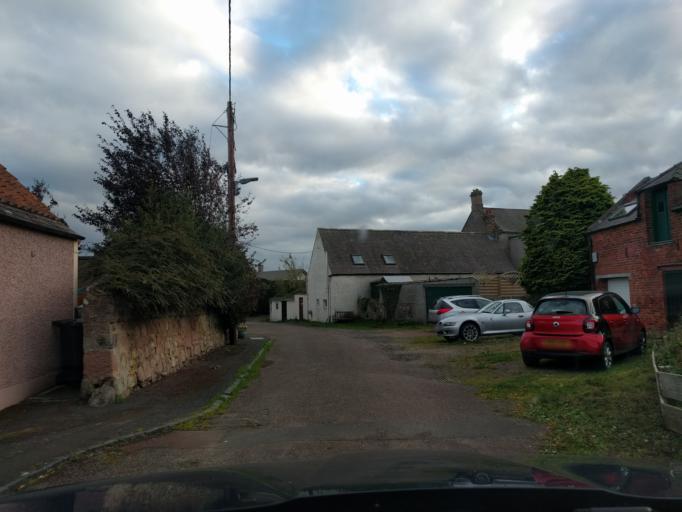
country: GB
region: Scotland
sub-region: The Scottish Borders
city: Allanton
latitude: 55.7408
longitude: -2.1151
